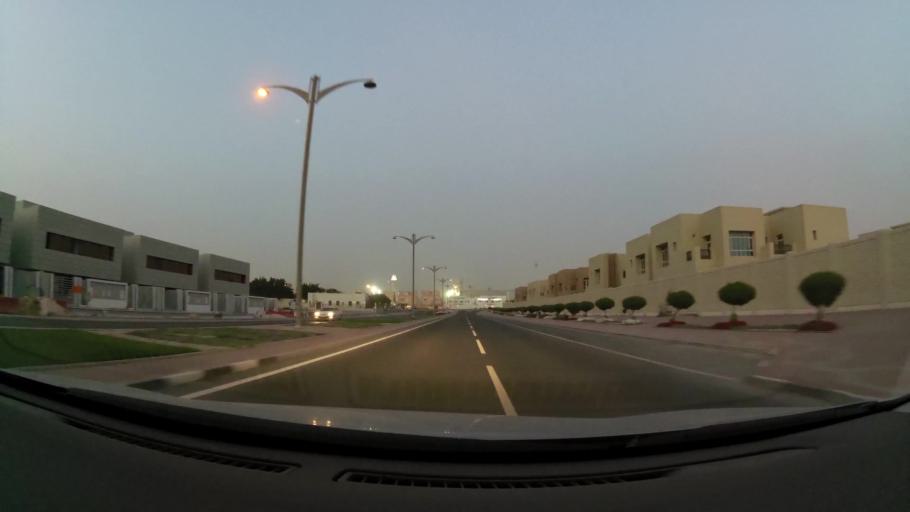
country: QA
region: Baladiyat ad Dawhah
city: Doha
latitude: 25.2648
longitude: 51.4755
